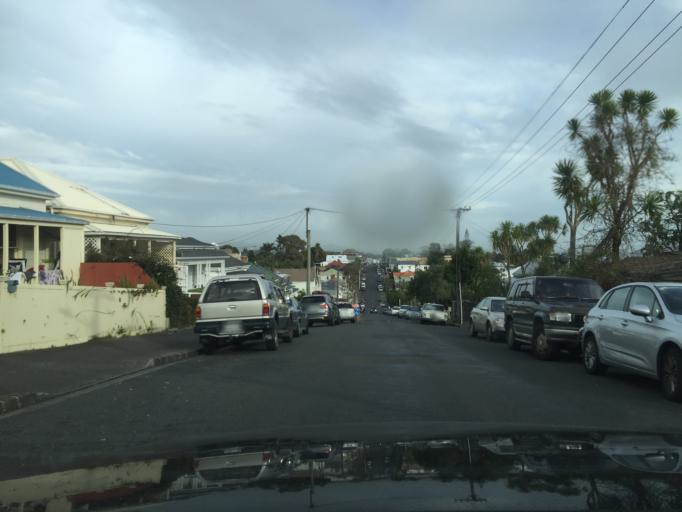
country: NZ
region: Auckland
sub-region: Auckland
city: Auckland
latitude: -36.8545
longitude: 174.7429
